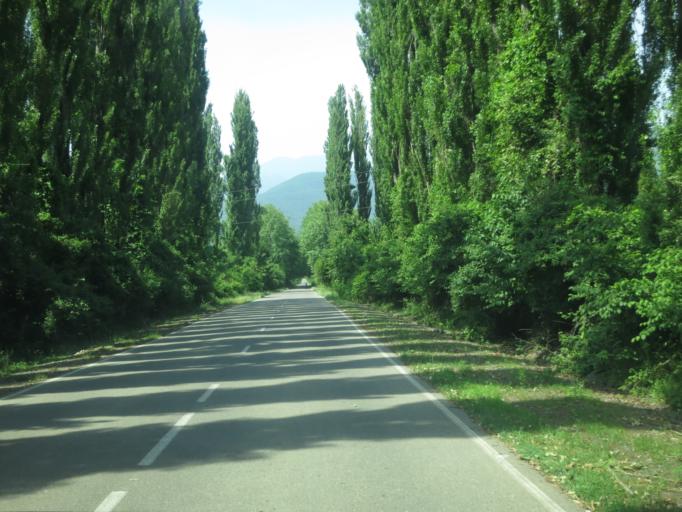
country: GE
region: Kakheti
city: Qvareli
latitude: 41.9506
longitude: 45.7501
